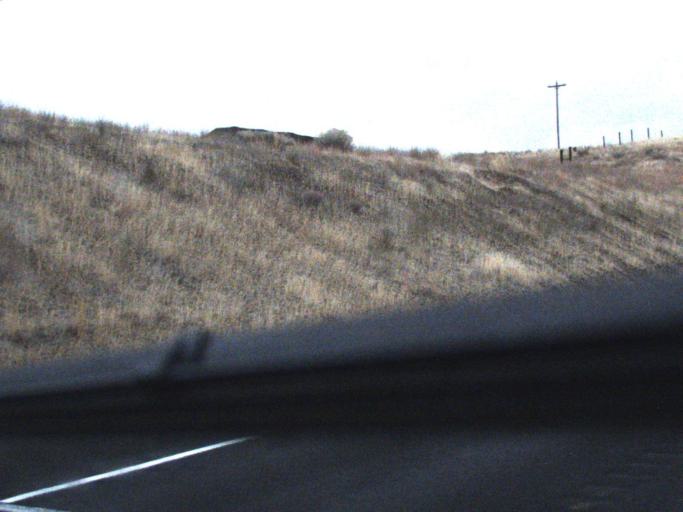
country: US
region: Washington
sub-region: Columbia County
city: Dayton
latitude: 46.7653
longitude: -118.0140
